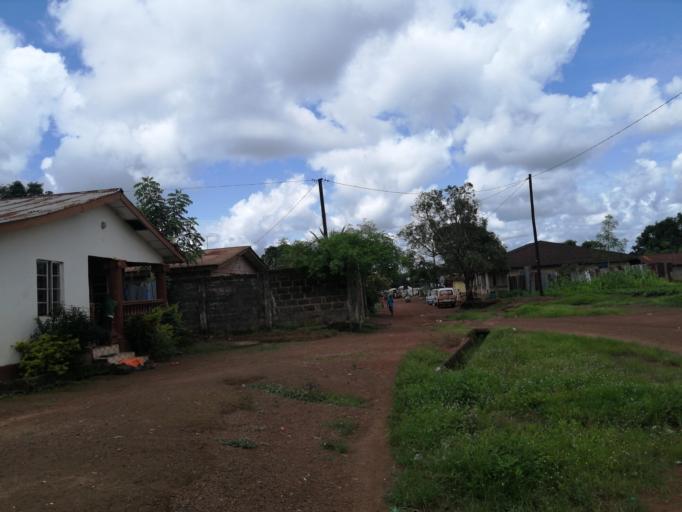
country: SL
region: Northern Province
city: Port Loko
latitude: 8.7740
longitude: -12.7895
